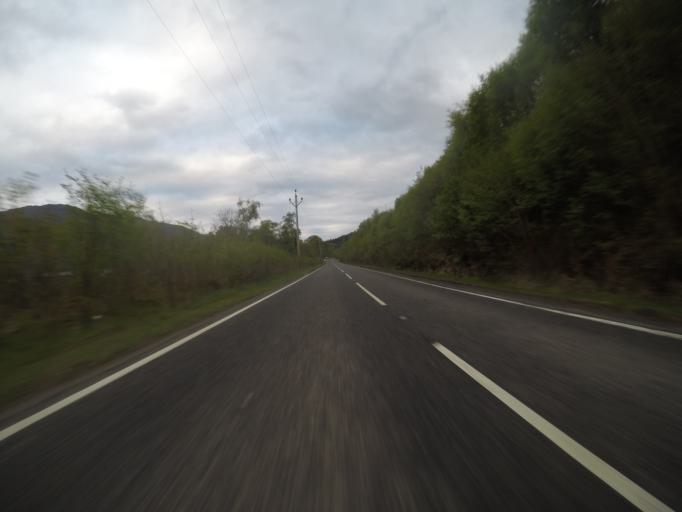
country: GB
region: Scotland
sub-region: Highland
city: Beauly
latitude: 57.1950
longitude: -4.6134
